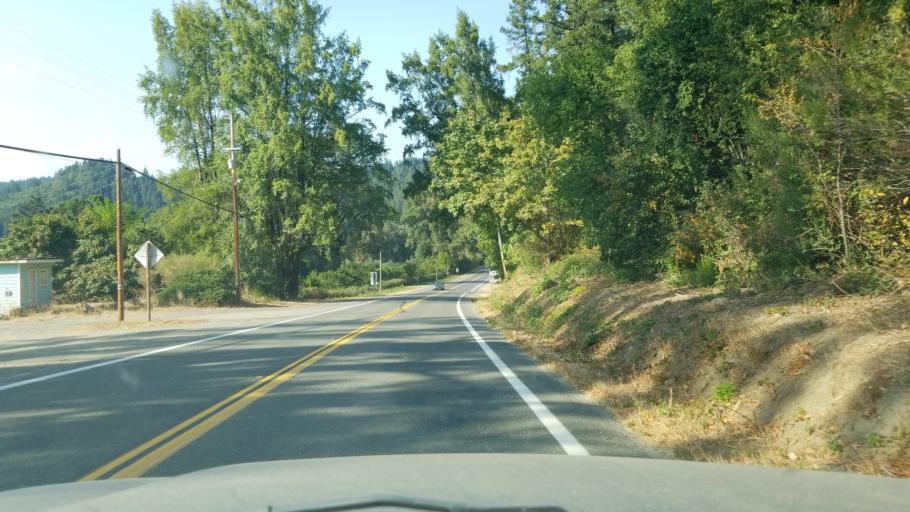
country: US
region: California
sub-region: Humboldt County
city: Redway
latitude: 40.2121
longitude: -123.7868
